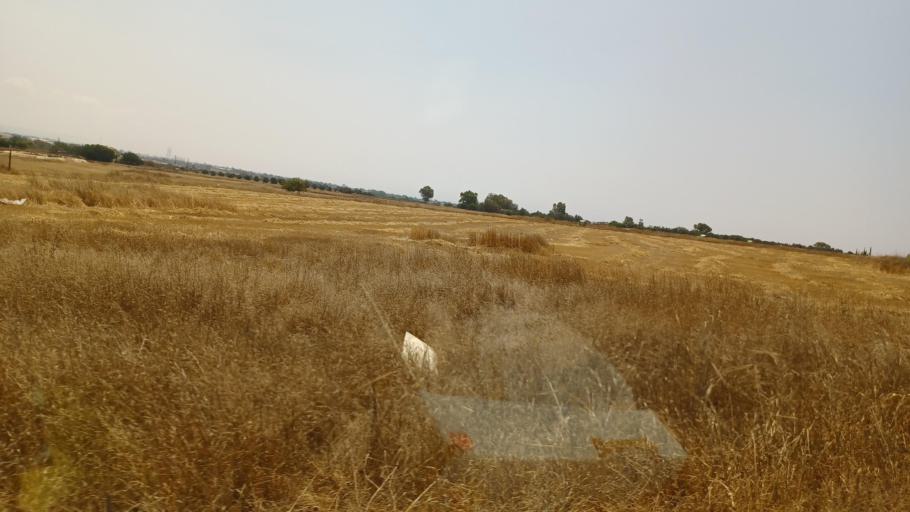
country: CY
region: Ammochostos
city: Liopetri
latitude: 34.9832
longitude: 33.8666
